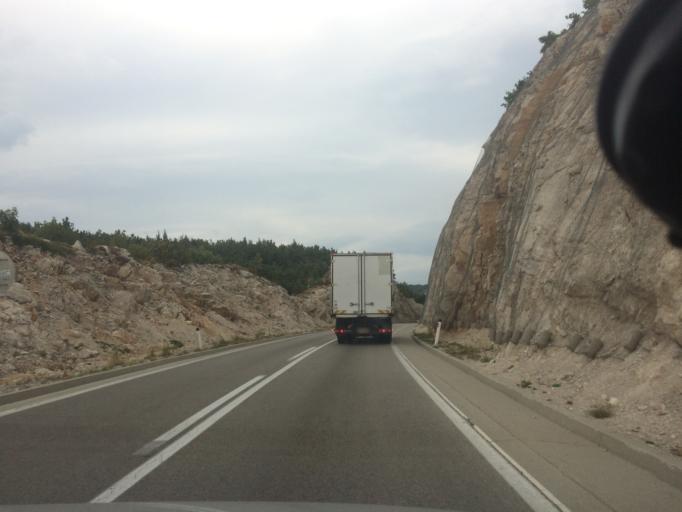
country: ME
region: Kotor
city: Risan
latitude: 42.6839
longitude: 18.6340
